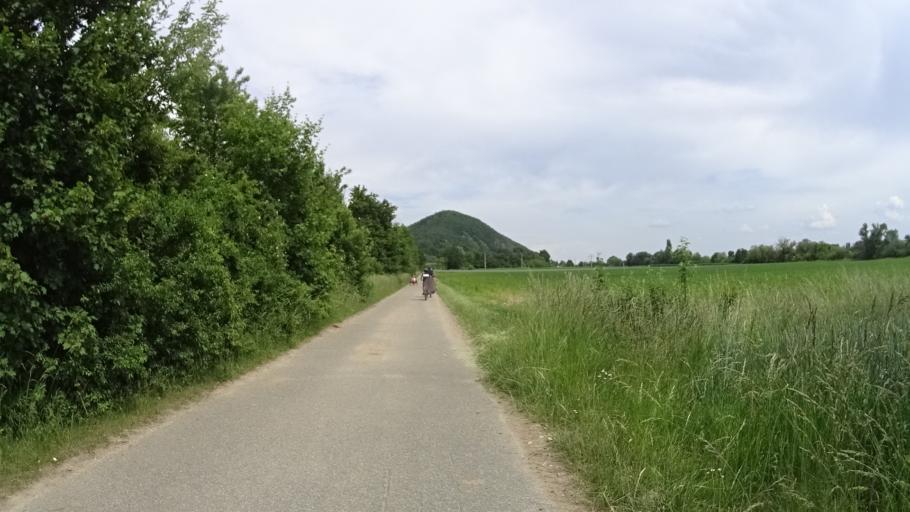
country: DE
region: Bavaria
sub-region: Upper Palatinate
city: Donaustauf
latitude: 49.0289
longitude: 12.2283
